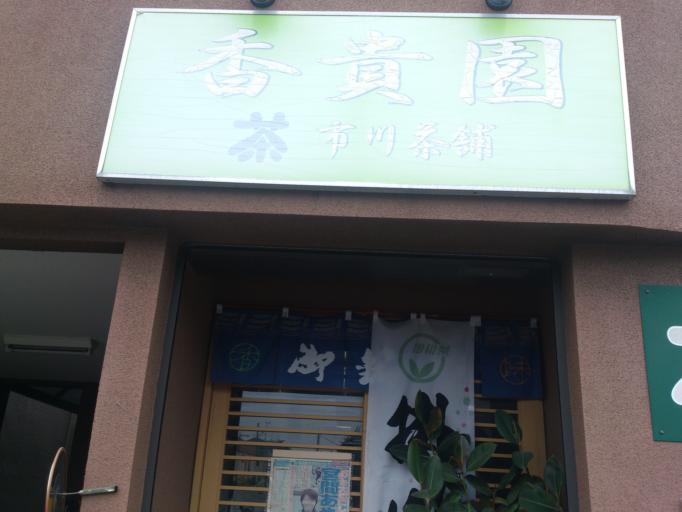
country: JP
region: Chiba
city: Chiba
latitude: 35.6517
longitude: 140.0649
